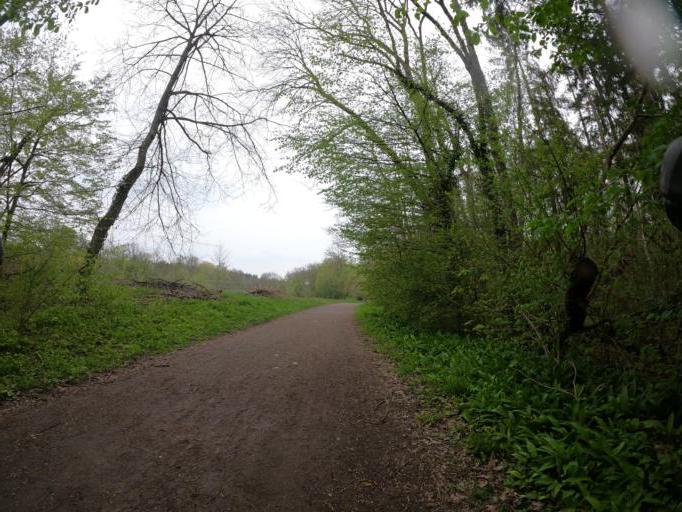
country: DE
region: Baden-Wuerttemberg
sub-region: Karlsruhe Region
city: Illingen
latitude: 48.9699
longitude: 8.9117
